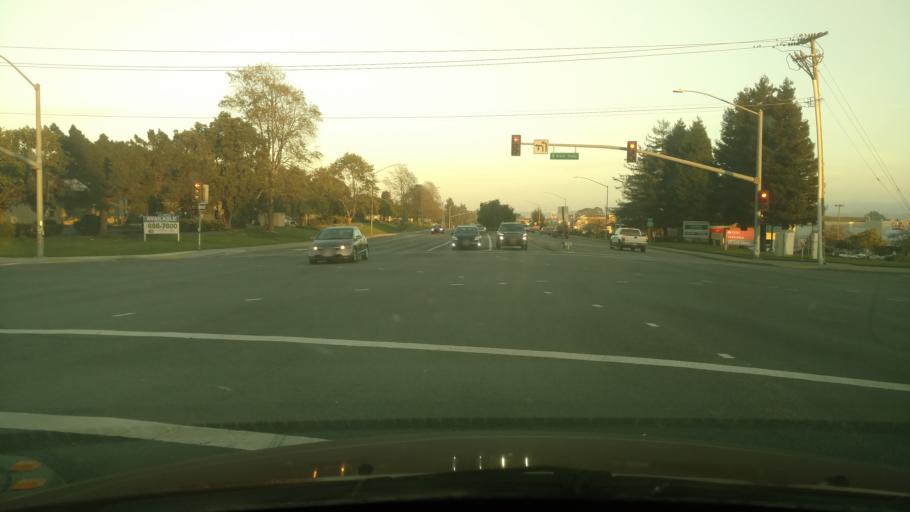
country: US
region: California
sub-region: Santa Cruz County
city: Freedom
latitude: 36.9187
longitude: -121.7842
